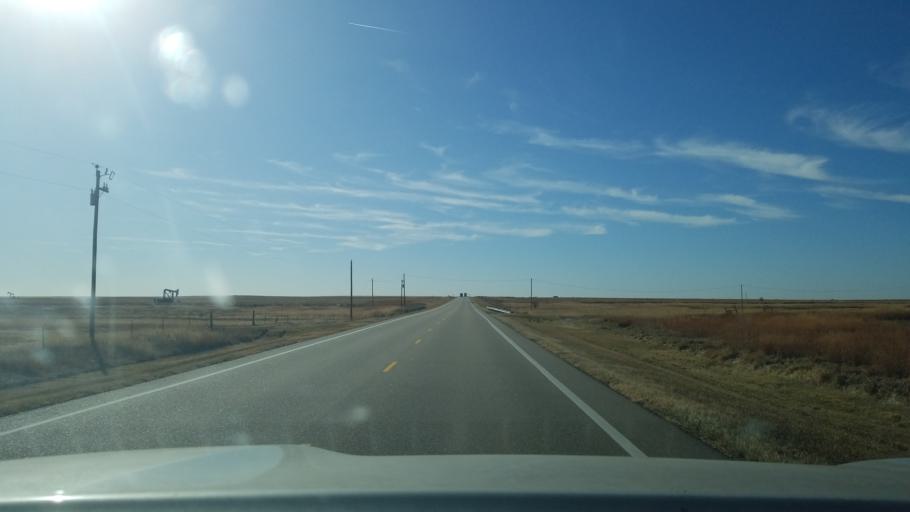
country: US
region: Kansas
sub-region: Ness County
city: Ness City
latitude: 38.3559
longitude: -99.8979
